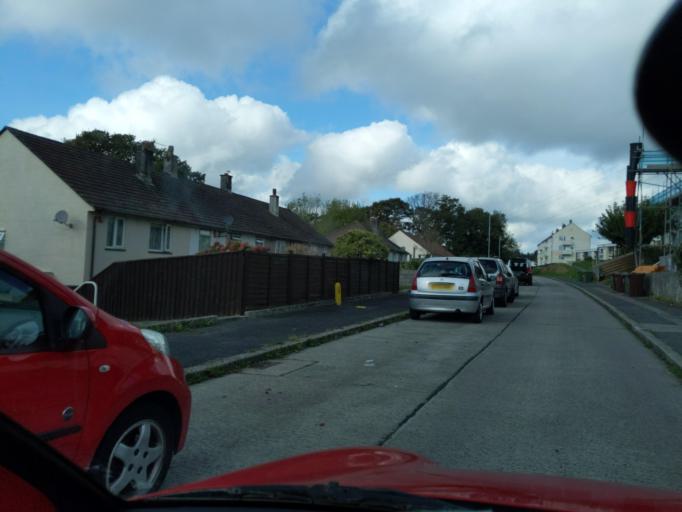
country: GB
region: England
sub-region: Plymouth
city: Plymouth
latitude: 50.4202
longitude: -4.1625
